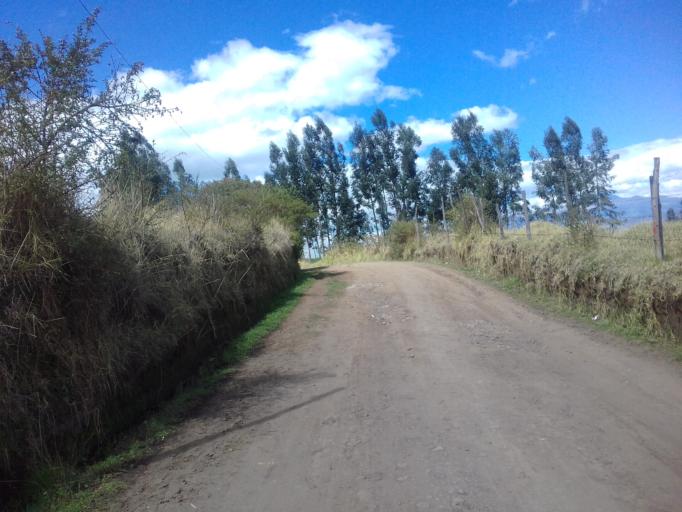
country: EC
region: Pichincha
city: Sangolqui
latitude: -0.3514
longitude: -78.4054
